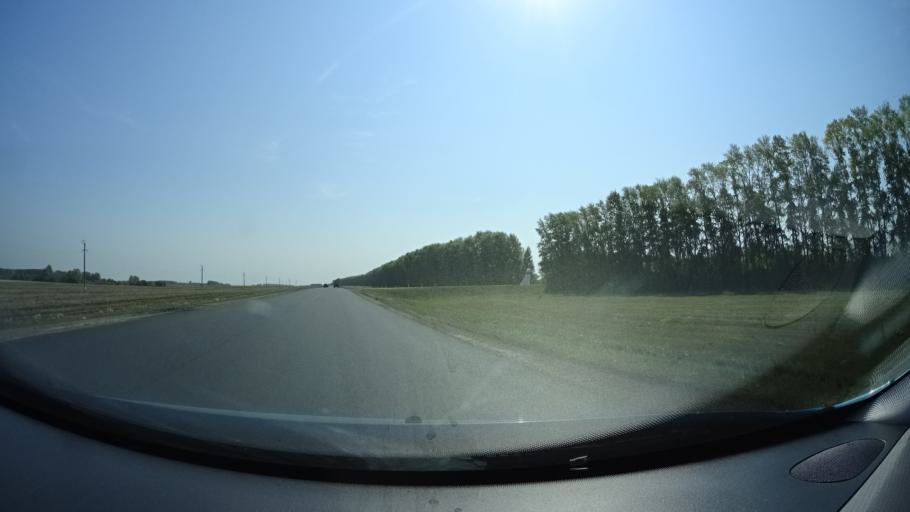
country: RU
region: Bashkortostan
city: Karmaskaly
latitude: 54.4094
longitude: 56.0705
